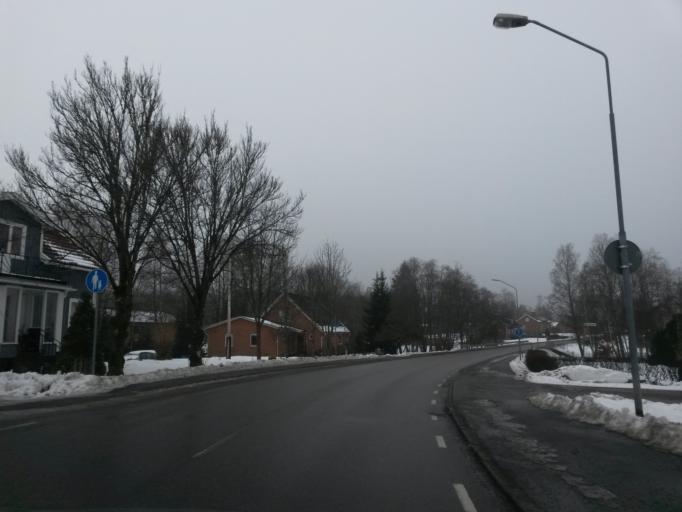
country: SE
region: Vaestra Goetaland
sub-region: Ulricehamns Kommun
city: Ulricehamn
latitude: 57.6667
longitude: 13.4289
